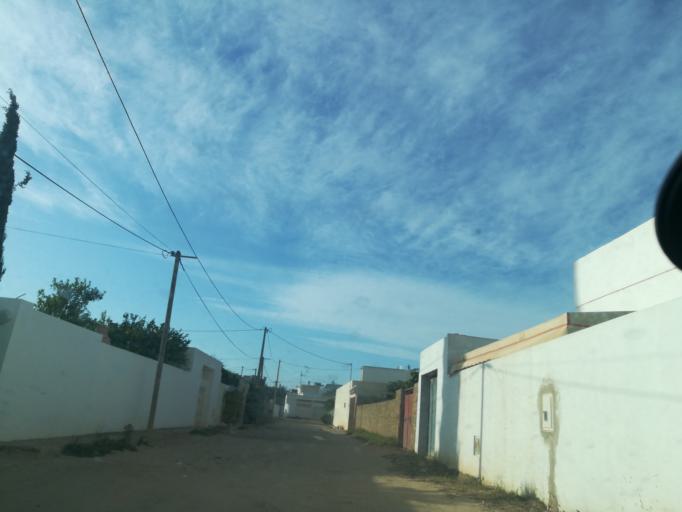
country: TN
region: Safaqis
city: Al Qarmadah
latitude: 34.8096
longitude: 10.7610
